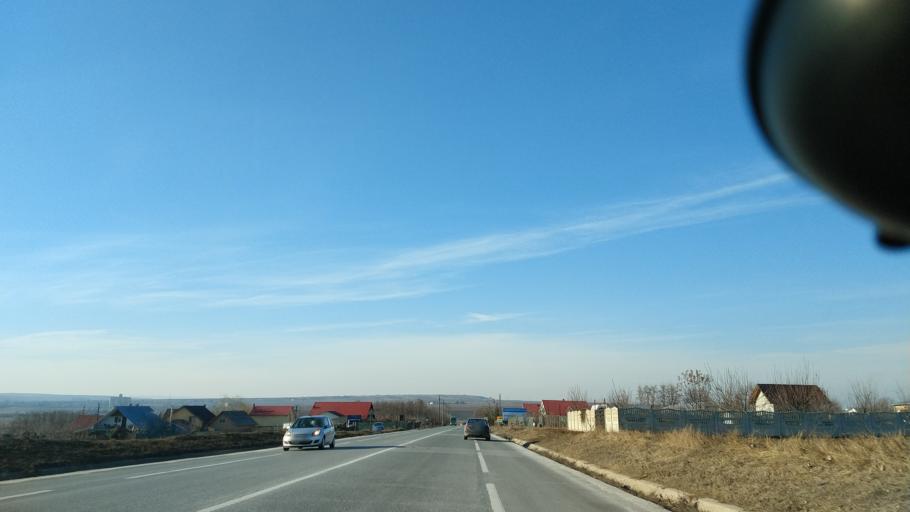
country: RO
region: Iasi
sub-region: Comuna Podu Iloaiei
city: Budai
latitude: 47.2244
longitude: 27.1900
